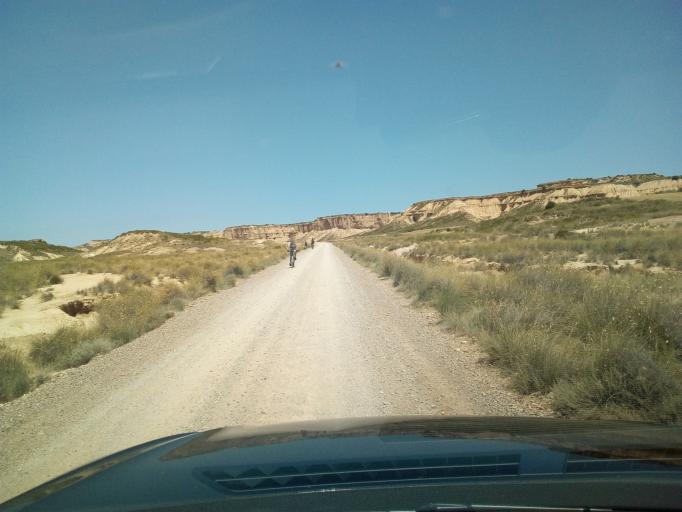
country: ES
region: Aragon
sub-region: Provincia de Zaragoza
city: Sadaba
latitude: 42.1885
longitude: -1.4118
